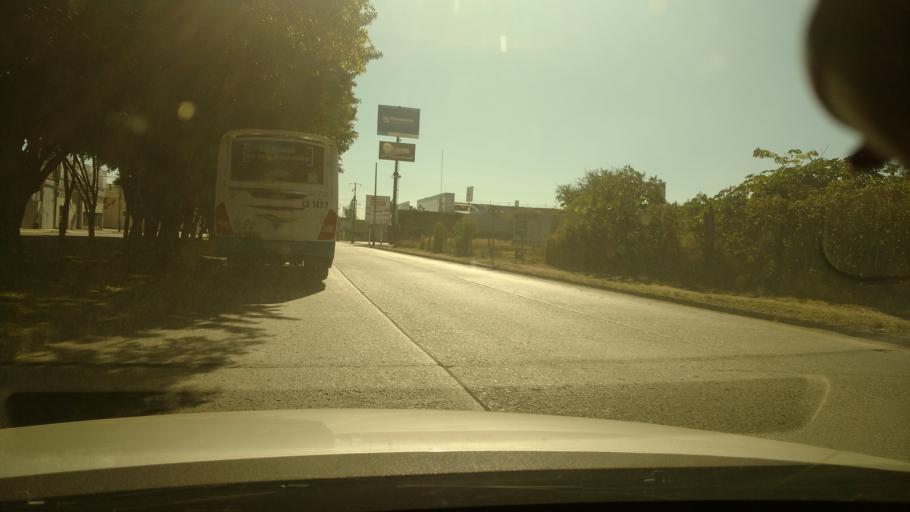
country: MX
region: Guanajuato
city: Leon
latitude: 21.1473
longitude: -101.6742
